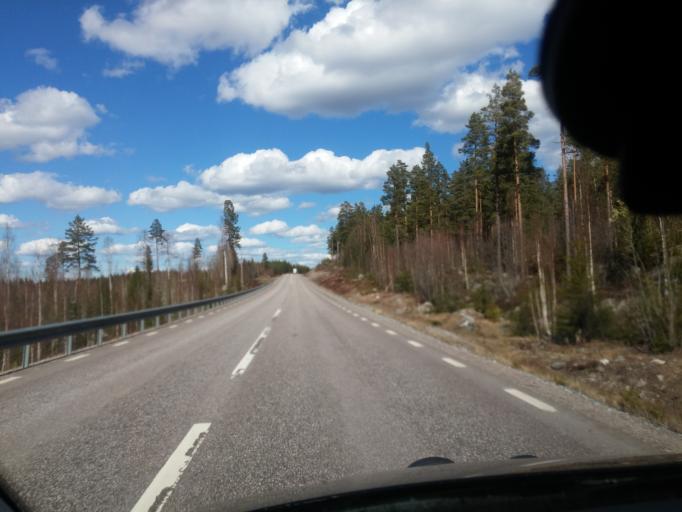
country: SE
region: Gaevleborg
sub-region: Ovanakers Kommun
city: Edsbyn
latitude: 61.2413
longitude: 15.8824
